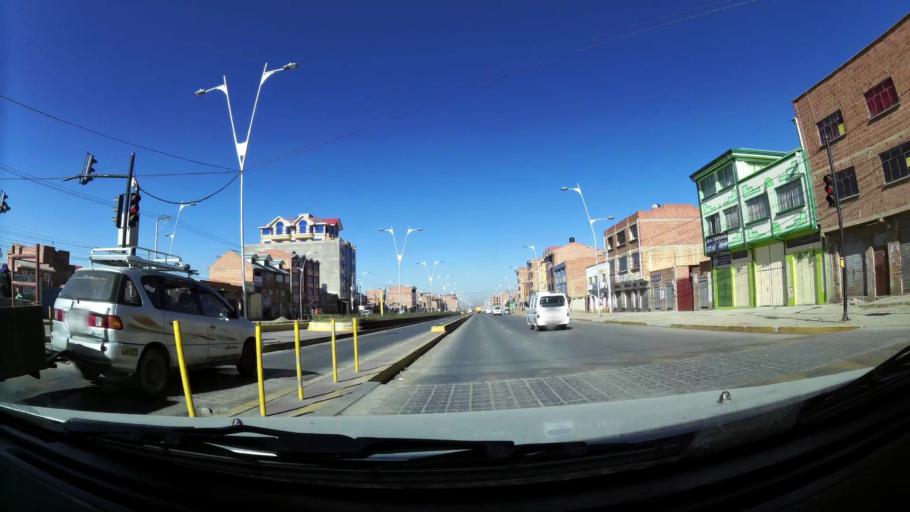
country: BO
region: La Paz
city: La Paz
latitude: -16.5280
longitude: -68.1856
